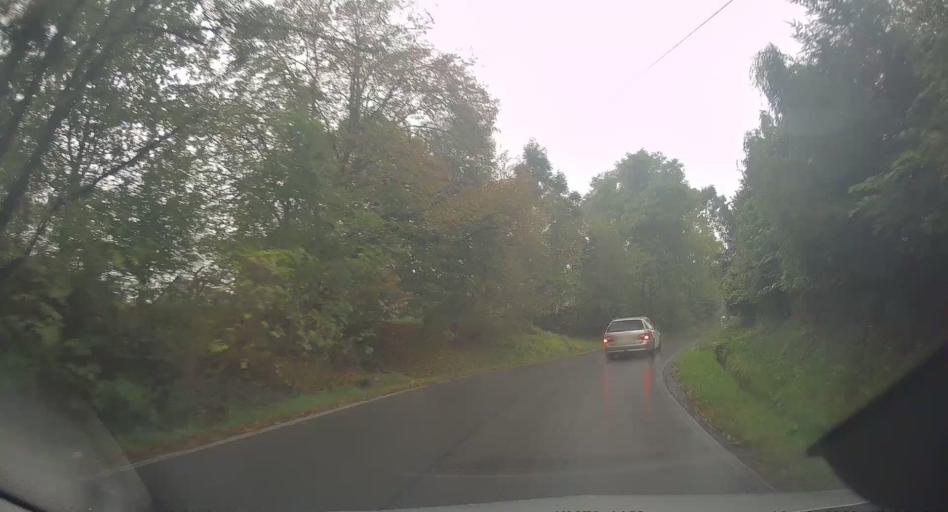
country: PL
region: Lesser Poland Voivodeship
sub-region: Powiat krakowski
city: Ochojno
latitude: 49.9600
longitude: 19.9997
